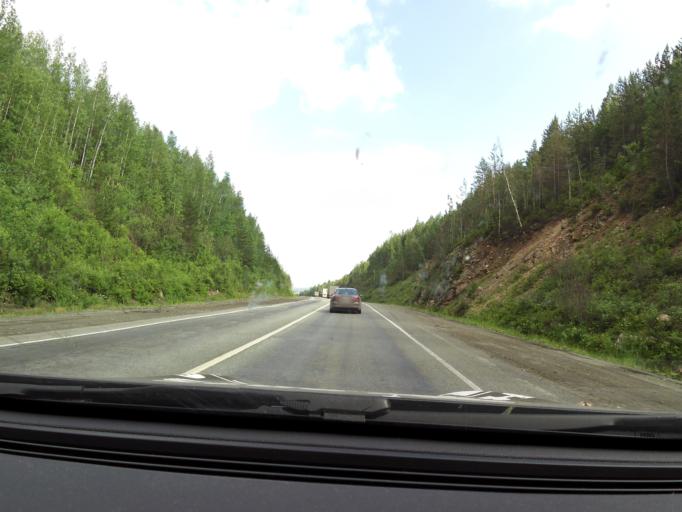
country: RU
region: Sverdlovsk
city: Revda
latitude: 56.8358
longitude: 59.8342
